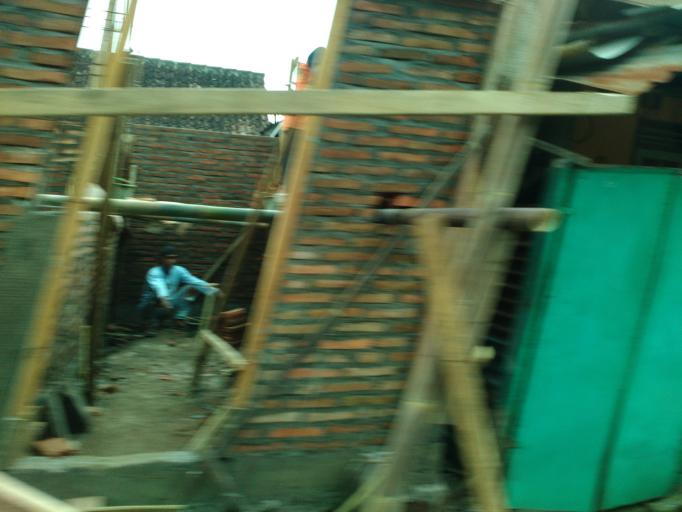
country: ID
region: Central Java
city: Gatak
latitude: -7.6053
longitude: 110.7017
